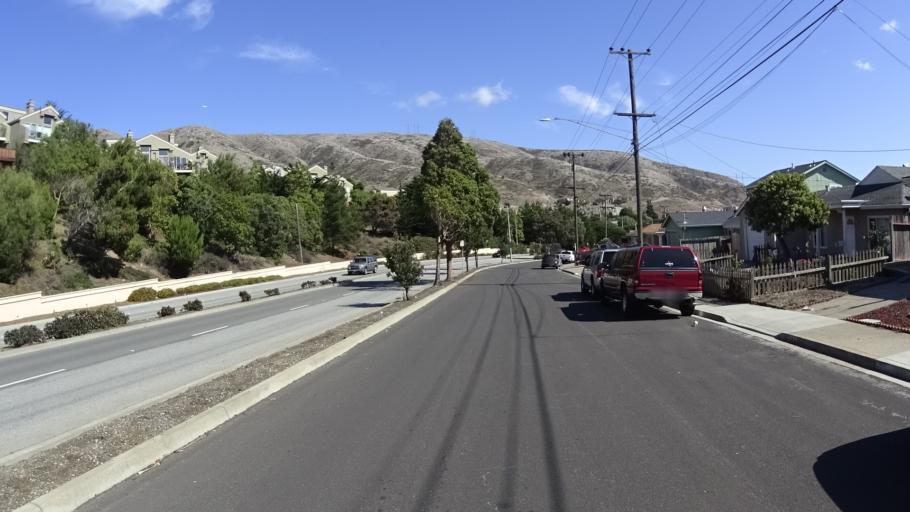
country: US
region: California
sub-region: San Mateo County
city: South San Francisco
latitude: 37.6694
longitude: -122.4206
